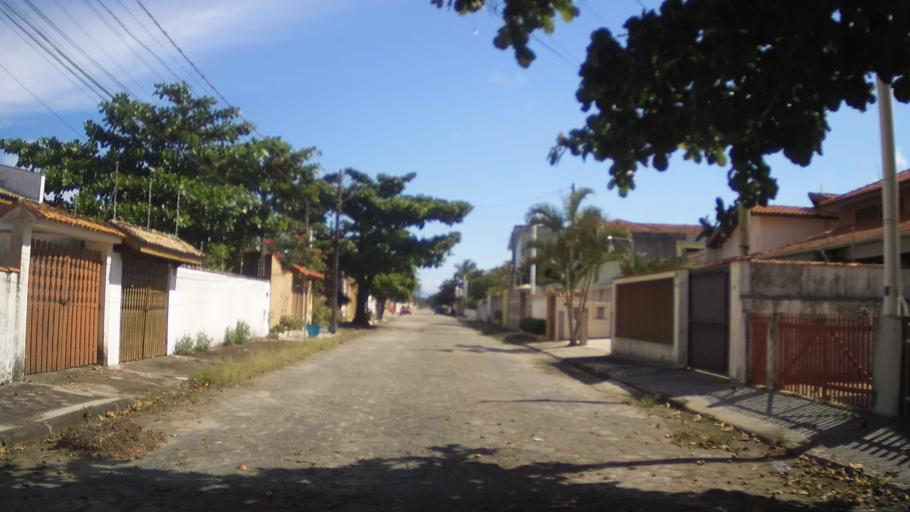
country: BR
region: Sao Paulo
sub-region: Itanhaem
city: Itanhaem
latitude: -24.1639
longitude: -46.7487
